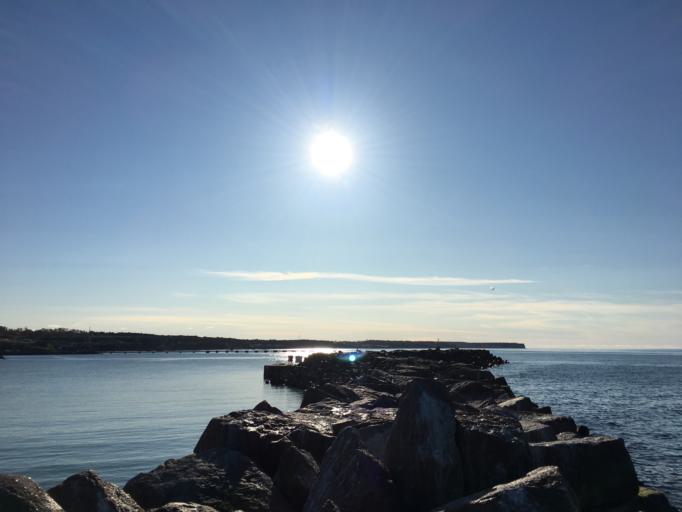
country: SE
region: Gotland
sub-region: Gotland
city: Visby
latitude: 57.6366
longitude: 18.2729
